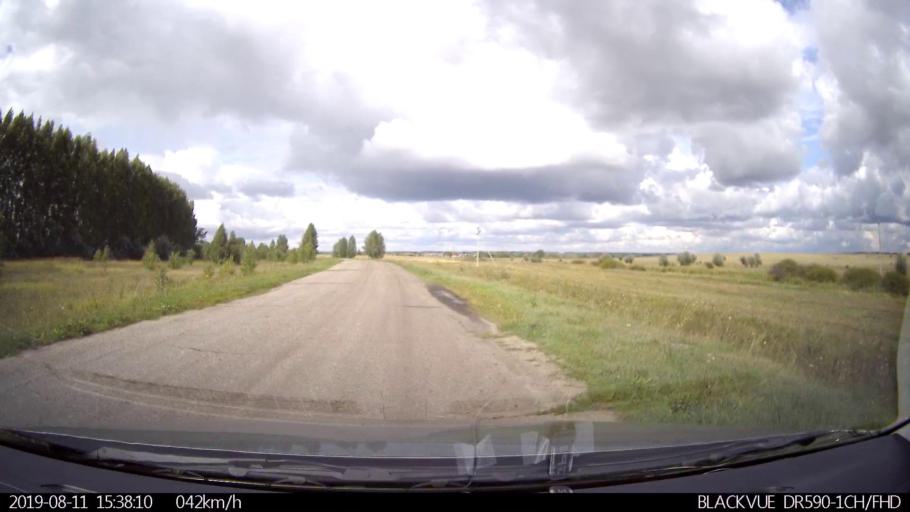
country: RU
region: Ulyanovsk
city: Ignatovka
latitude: 53.8596
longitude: 47.6403
